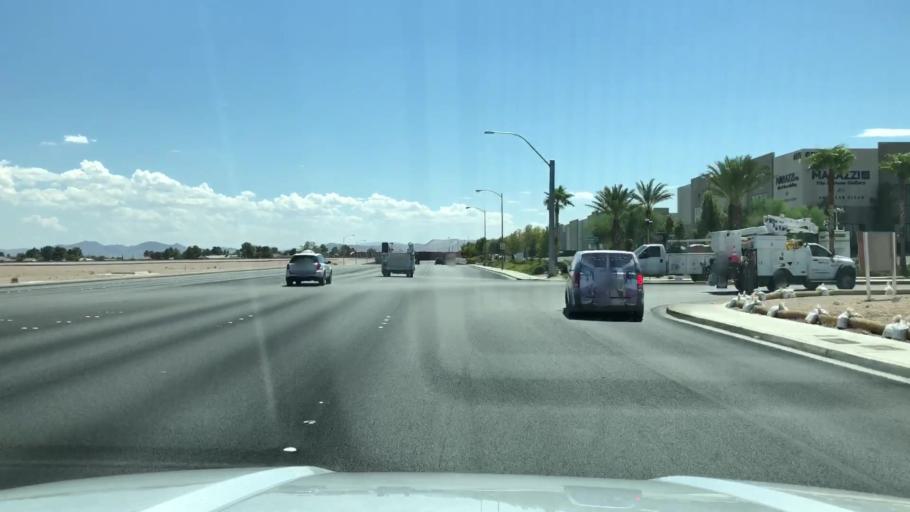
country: US
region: Nevada
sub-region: Clark County
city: Enterprise
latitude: 36.0637
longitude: -115.2083
